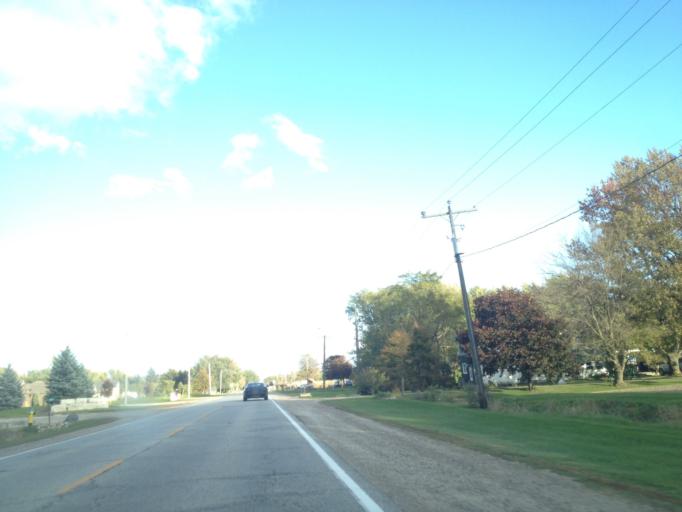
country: US
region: Michigan
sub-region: Wayne County
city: Grosse Pointe Farms
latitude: 42.2970
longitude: -82.6595
